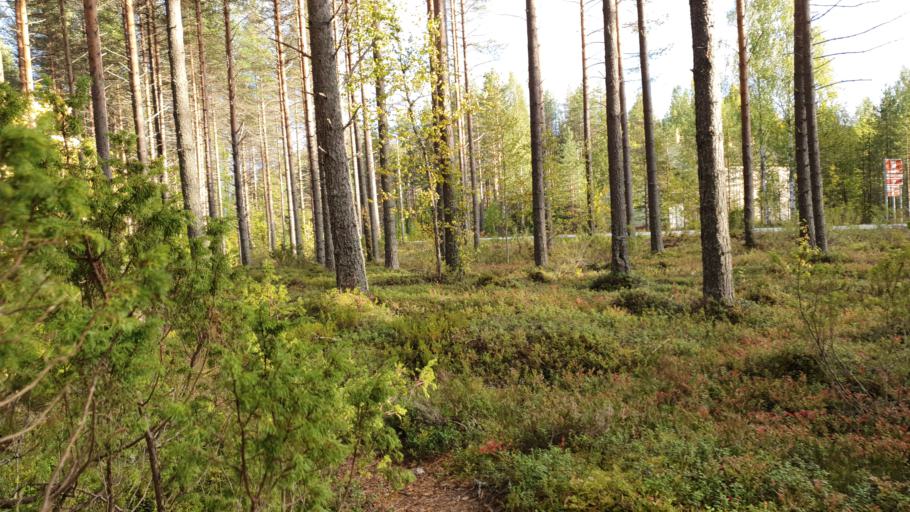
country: FI
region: Kainuu
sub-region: Kehys-Kainuu
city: Kuhmo
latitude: 63.9323
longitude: 29.9701
